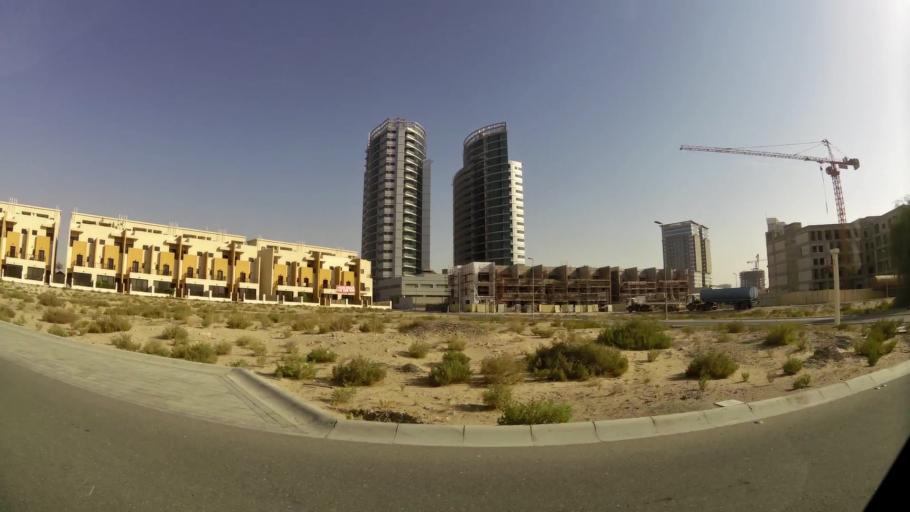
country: AE
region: Dubai
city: Dubai
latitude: 25.0524
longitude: 55.2177
